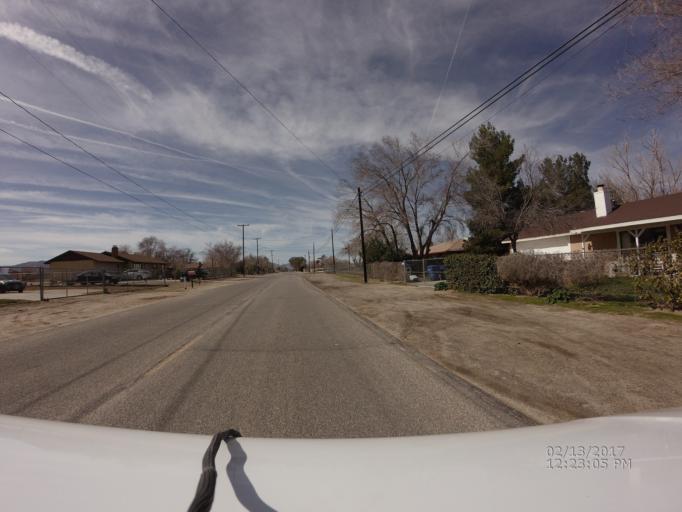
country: US
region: California
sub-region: Los Angeles County
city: Littlerock
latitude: 34.5653
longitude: -117.9424
